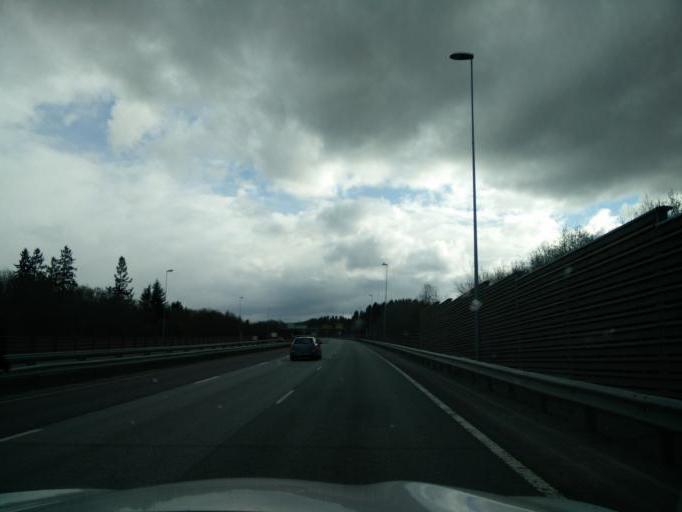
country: NO
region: Sor-Trondelag
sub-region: Trondheim
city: Trondheim
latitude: 63.3861
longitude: 10.3776
